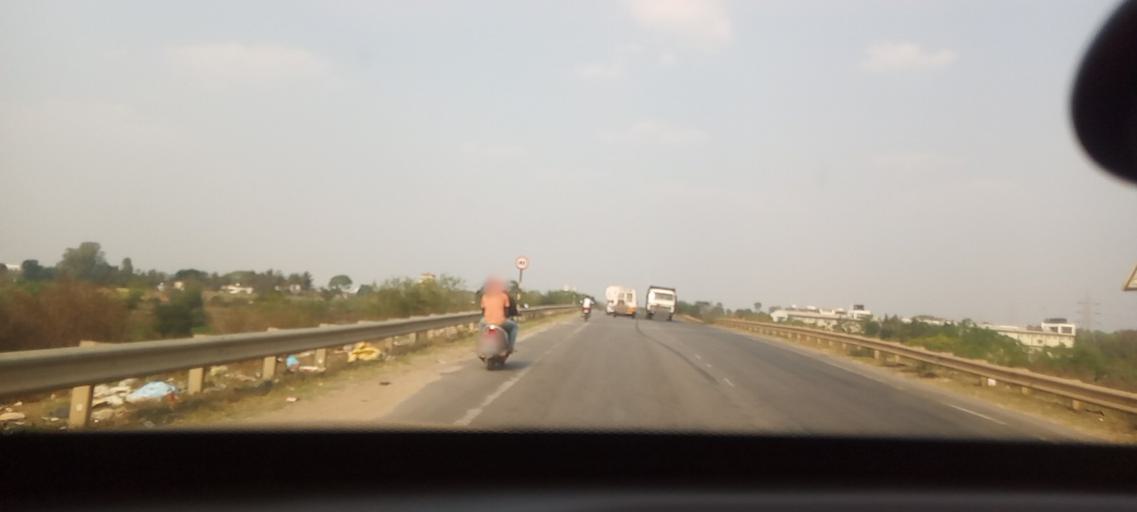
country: IN
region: Karnataka
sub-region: Hassan
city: Hassan
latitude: 12.9908
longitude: 76.1129
